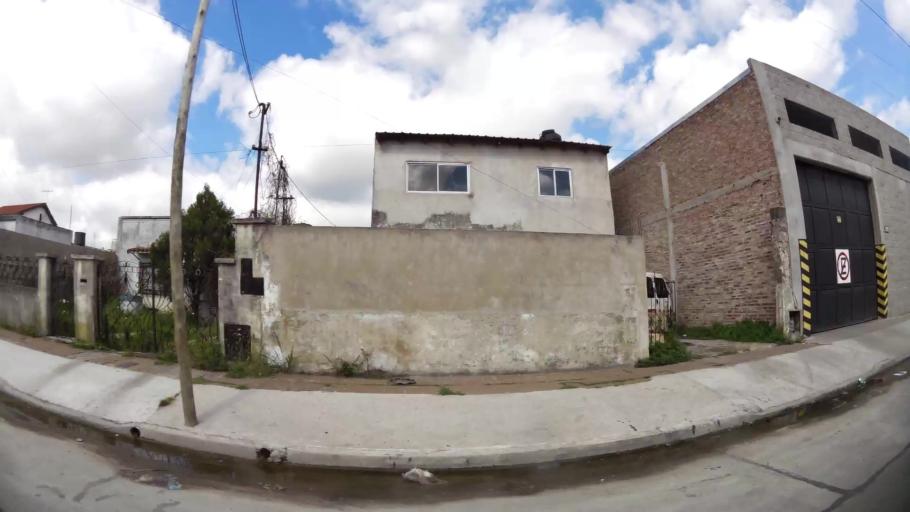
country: AR
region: Buenos Aires
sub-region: Partido de Lanus
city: Lanus
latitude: -34.6840
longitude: -58.4313
